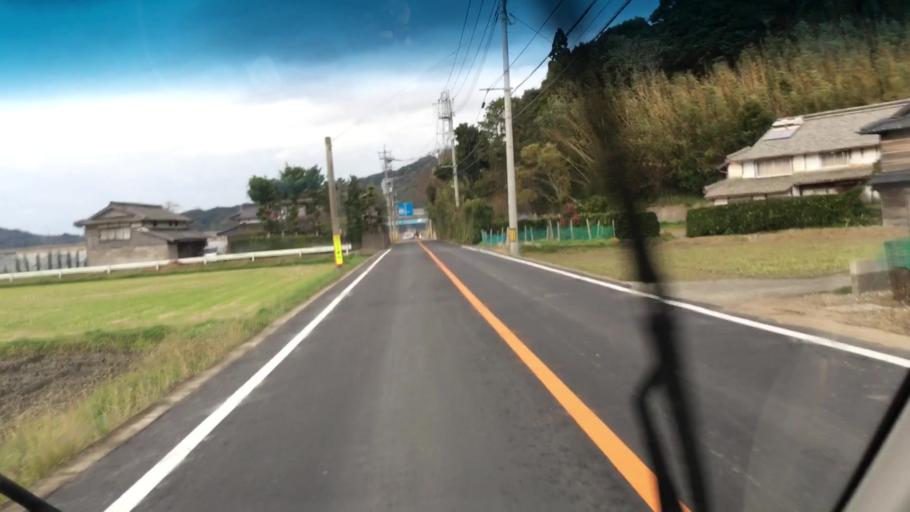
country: JP
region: Fukuoka
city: Maebaru-chuo
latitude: 33.5291
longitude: 130.1893
